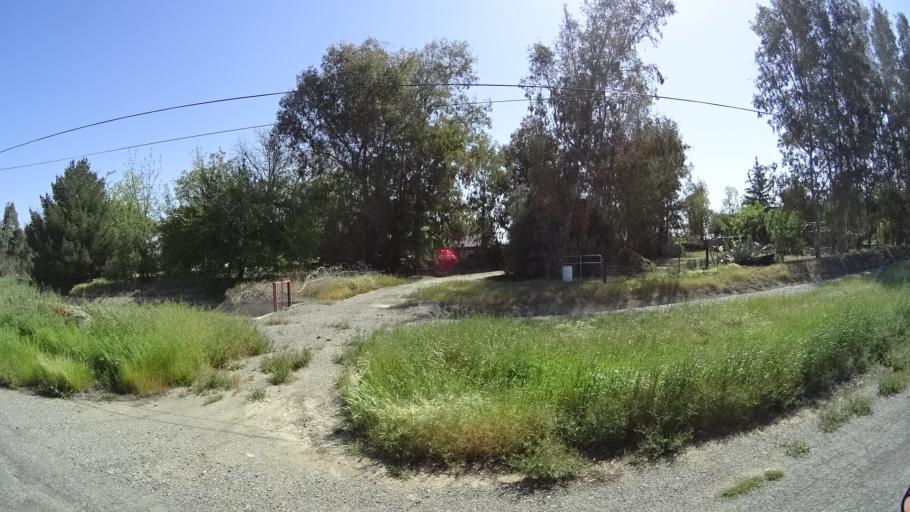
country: US
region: California
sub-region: Glenn County
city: Orland
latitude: 39.7278
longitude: -122.1960
